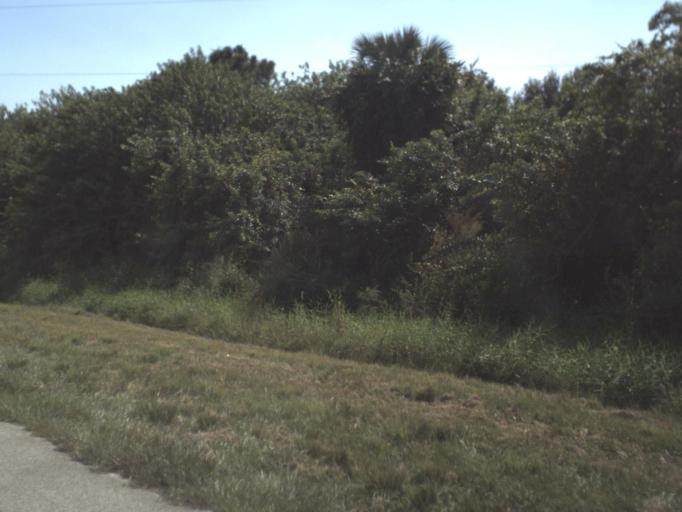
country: US
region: Florida
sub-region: Okeechobee County
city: Okeechobee
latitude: 27.2728
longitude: -80.8711
